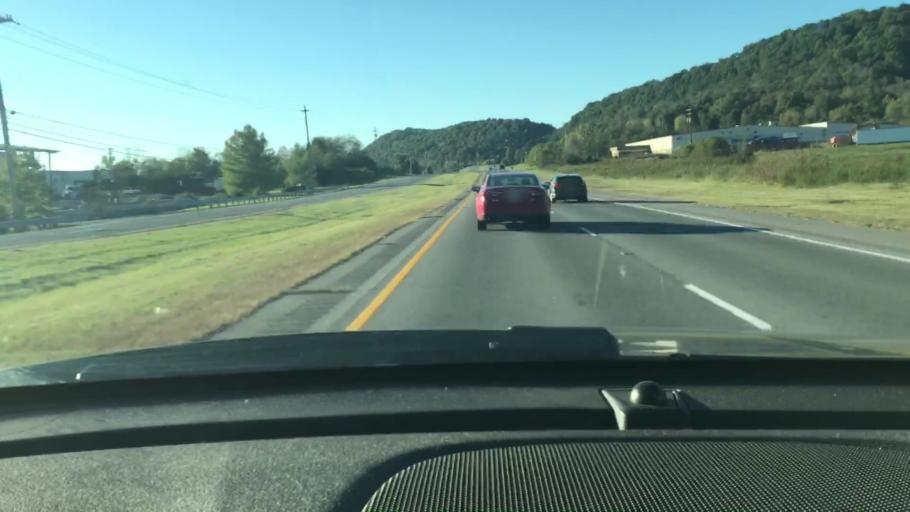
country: US
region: Tennessee
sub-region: Cheatham County
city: Ashland City
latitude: 36.2258
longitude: -87.0089
